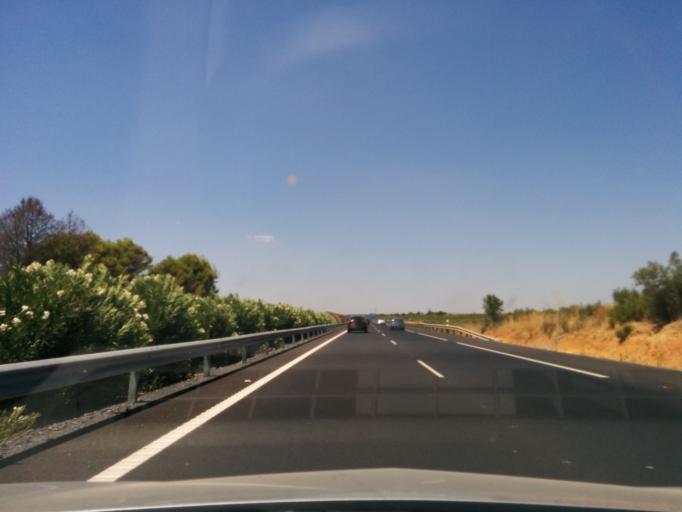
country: ES
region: Andalusia
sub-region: Provincia de Huelva
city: Chucena
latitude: 37.3537
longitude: -6.3760
